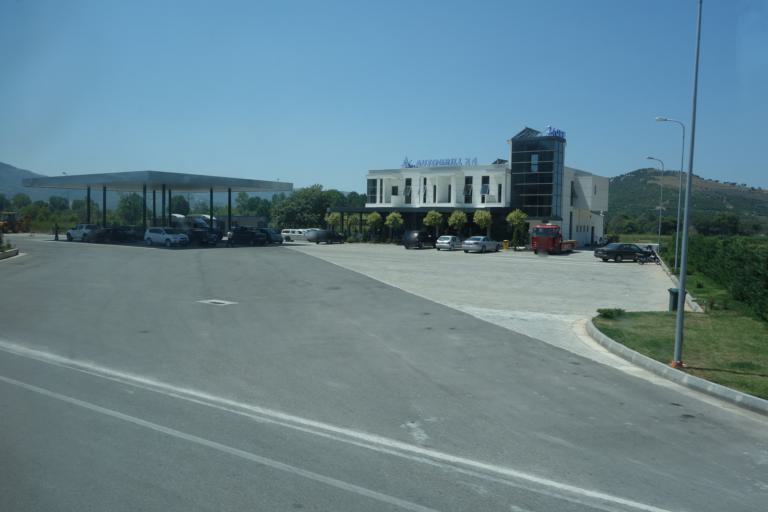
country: AL
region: Fier
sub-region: Rrethi i Mallakastres
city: Hekal
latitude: 40.5187
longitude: 19.7419
